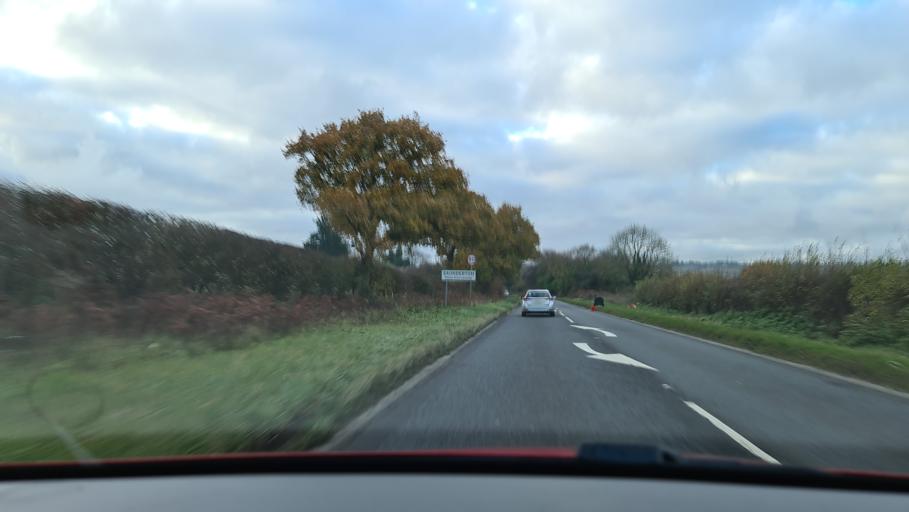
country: GB
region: England
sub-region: Buckinghamshire
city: Princes Risborough
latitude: 51.6944
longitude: -0.8323
